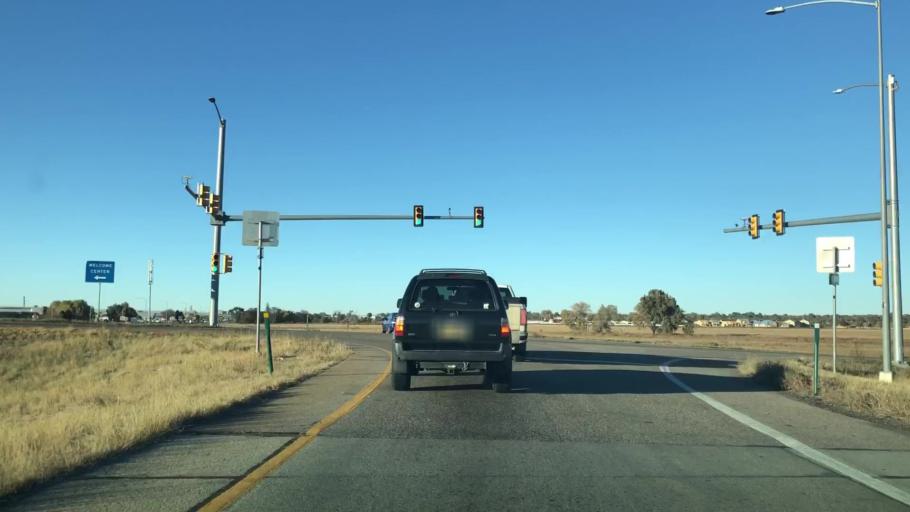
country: US
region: Colorado
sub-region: Larimer County
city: Fort Collins
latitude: 40.5662
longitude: -105.0005
